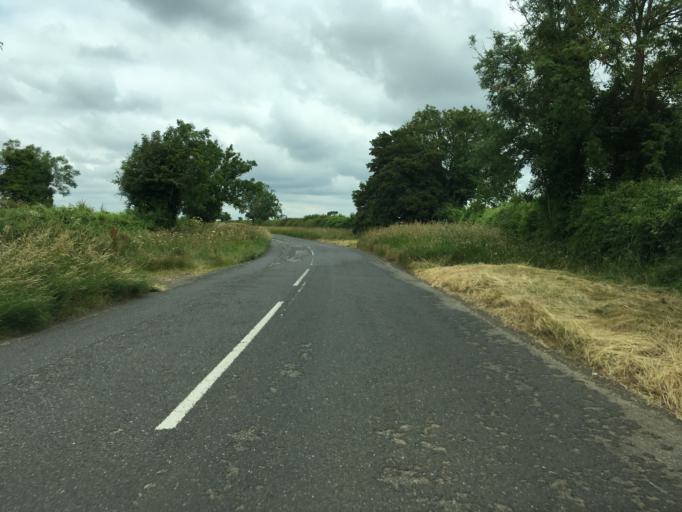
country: GB
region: England
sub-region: Oxfordshire
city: Charlbury
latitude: 51.9137
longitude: -1.4926
